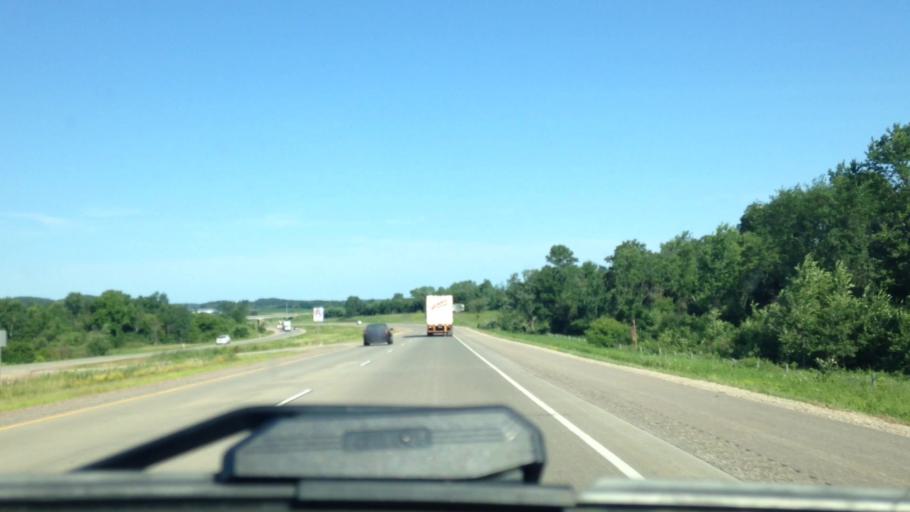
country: US
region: Wisconsin
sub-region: Trempealeau County
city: Osseo
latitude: 44.6175
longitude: -91.2479
